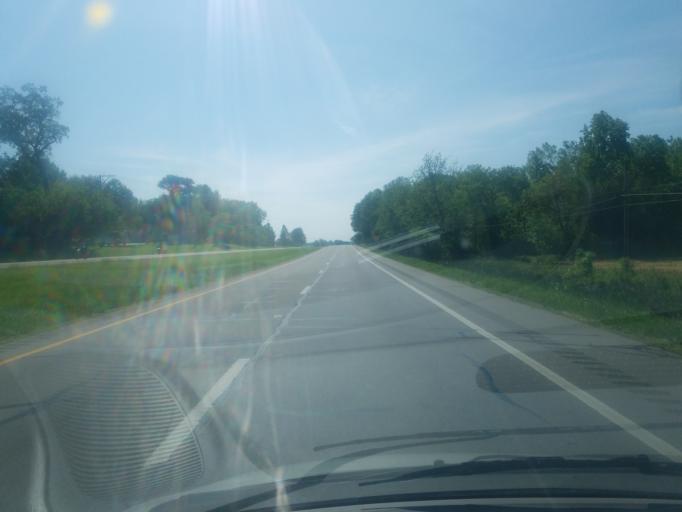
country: US
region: Ohio
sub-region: Huron County
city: Bellevue
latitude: 41.2615
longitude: -82.7692
